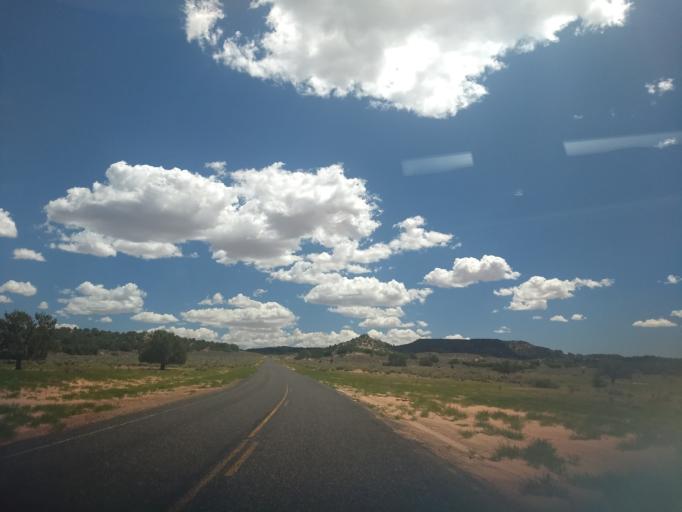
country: US
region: Utah
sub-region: Kane County
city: Kanab
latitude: 37.1458
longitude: -112.6741
